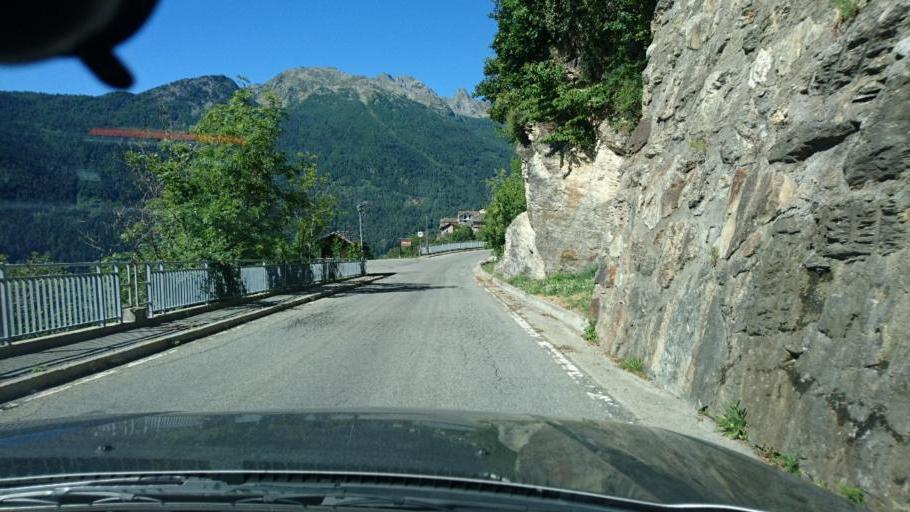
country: IT
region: Aosta Valley
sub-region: Valle d'Aosta
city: Avise
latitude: 45.7160
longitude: 7.1403
